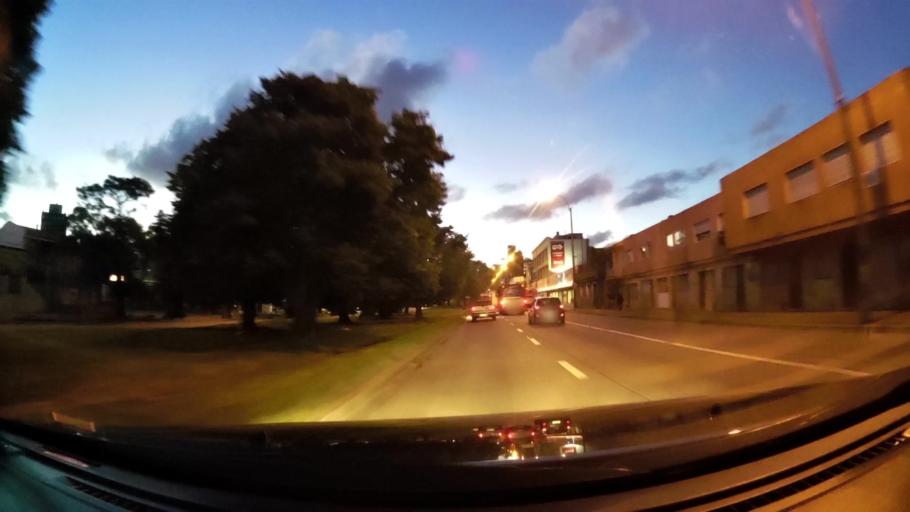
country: UY
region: Montevideo
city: Montevideo
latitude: -34.8866
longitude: -56.1338
